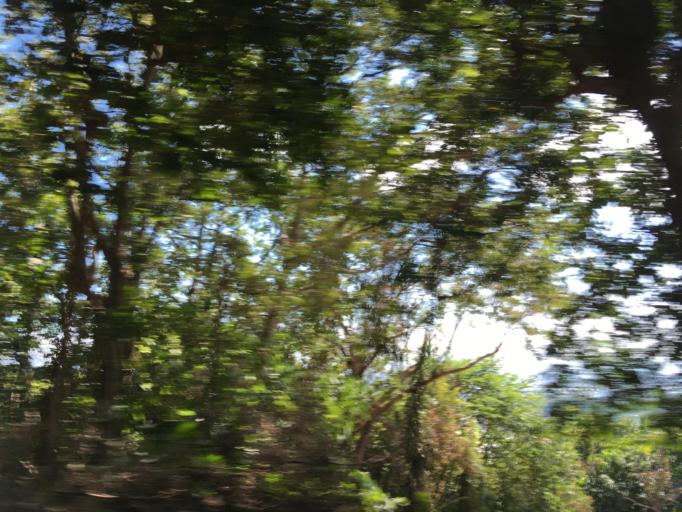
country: TW
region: Taipei
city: Taipei
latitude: 25.1511
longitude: 121.5041
